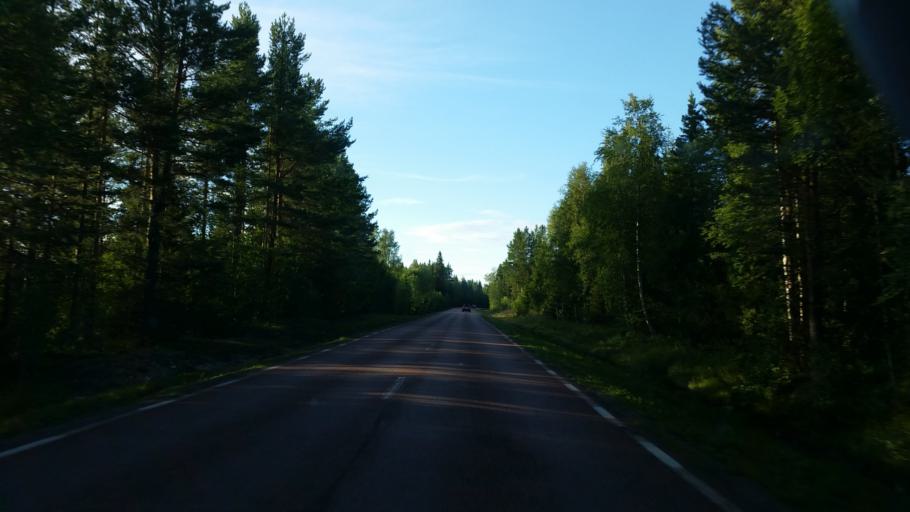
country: SE
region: Vaesterbotten
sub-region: Dorotea Kommun
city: Dorotea
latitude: 64.0901
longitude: 16.0856
